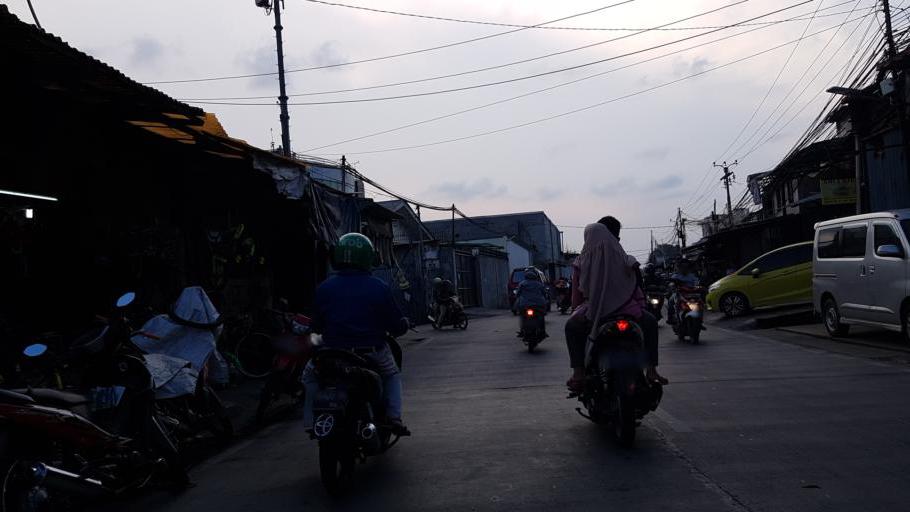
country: ID
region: Jakarta Raya
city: Jakarta
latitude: -6.1415
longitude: 106.7731
